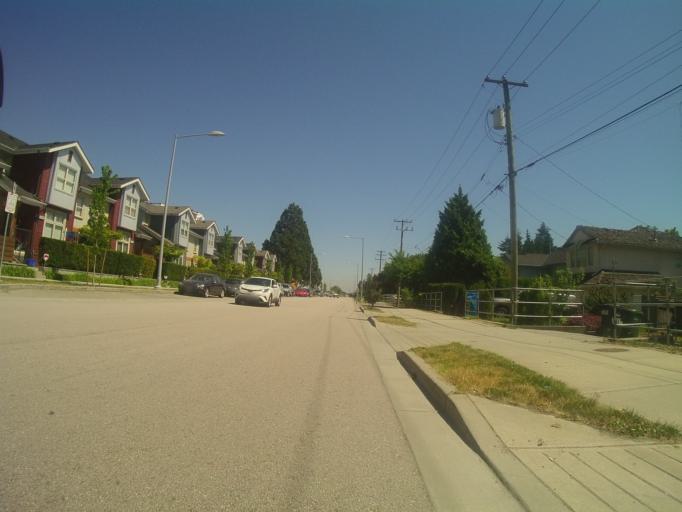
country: CA
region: British Columbia
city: Richmond
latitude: 49.1988
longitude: -123.1123
